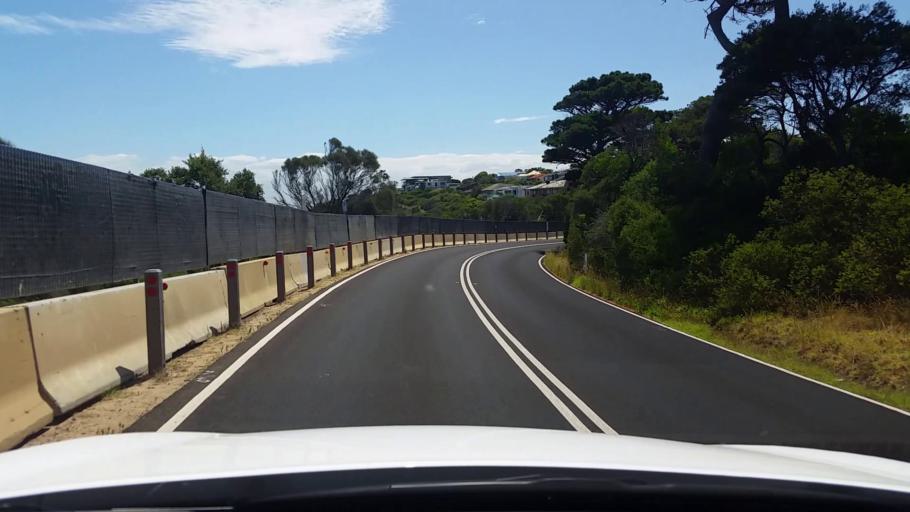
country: AU
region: Victoria
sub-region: Mornington Peninsula
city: Mount Martha
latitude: -38.2768
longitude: 145.0007
